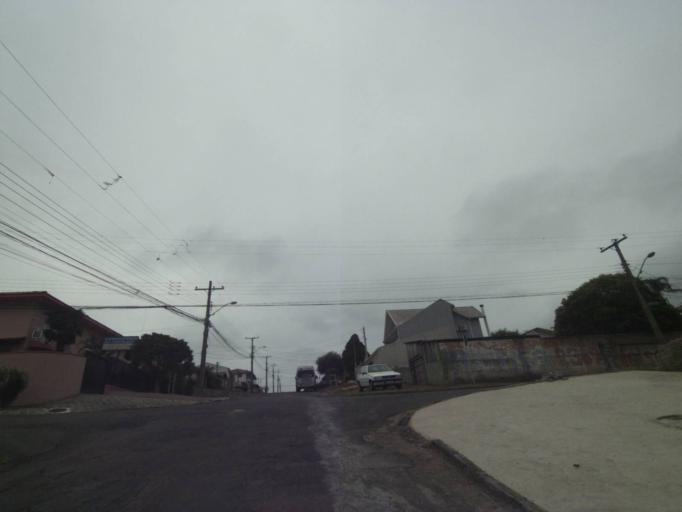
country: BR
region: Parana
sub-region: Sao Jose Dos Pinhais
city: Sao Jose dos Pinhais
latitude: -25.4826
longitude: -49.2335
